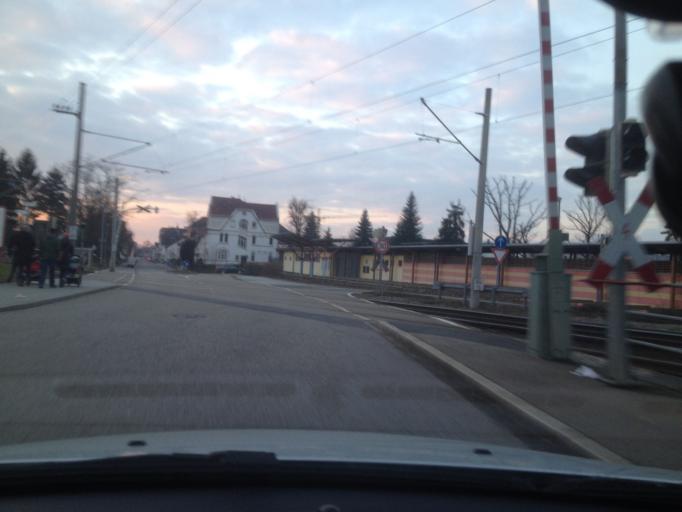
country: DE
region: Baden-Wuerttemberg
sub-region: Karlsruhe Region
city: Ettlingen
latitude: 48.9364
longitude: 8.4174
